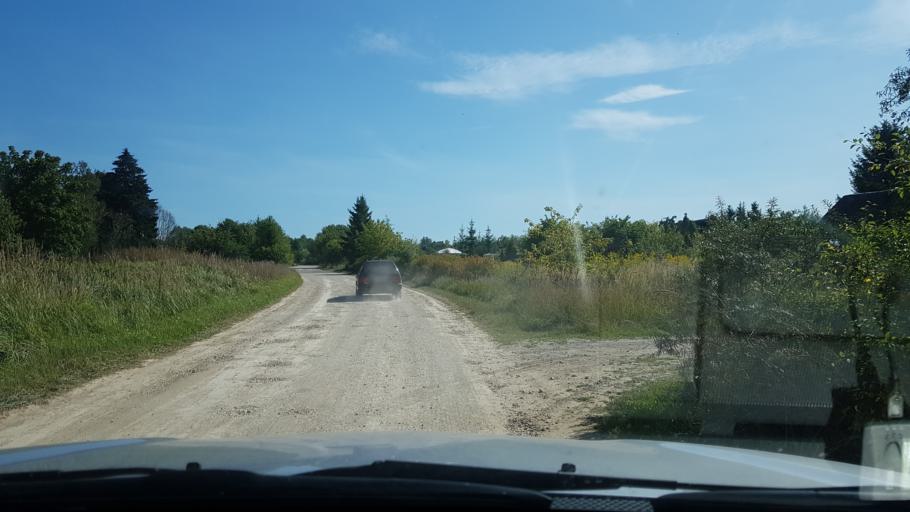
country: EE
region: Ida-Virumaa
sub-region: Sillamaee linn
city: Sillamae
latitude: 59.3727
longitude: 27.7880
